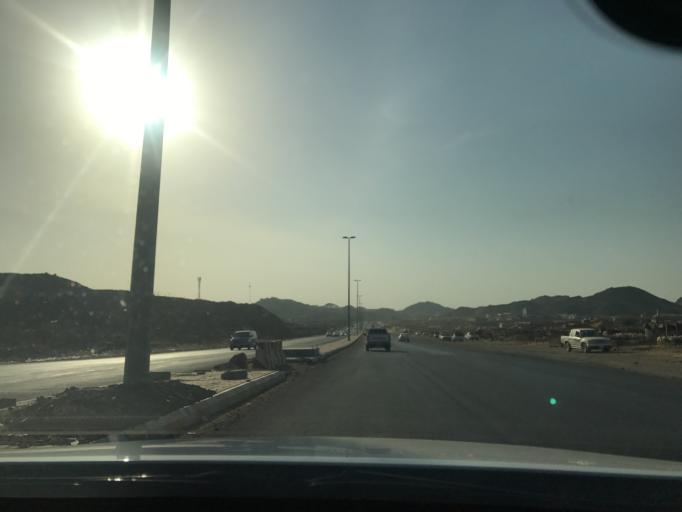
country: SA
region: Makkah
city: Jeddah
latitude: 21.4134
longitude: 39.4180
